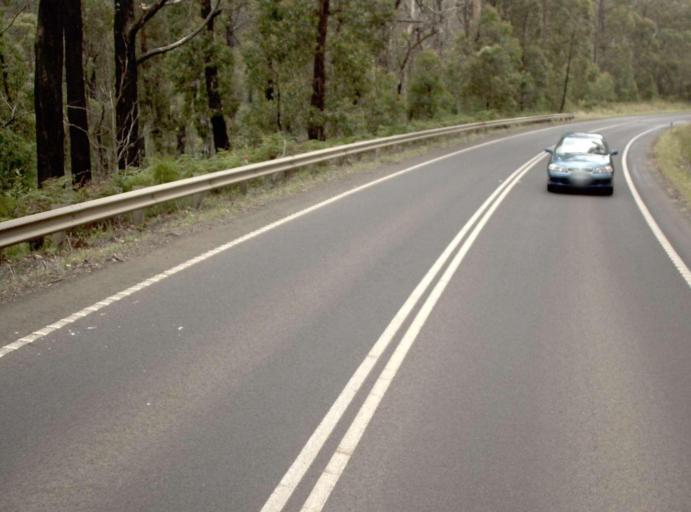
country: AU
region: Victoria
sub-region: Latrobe
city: Moe
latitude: -38.3671
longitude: 146.1774
